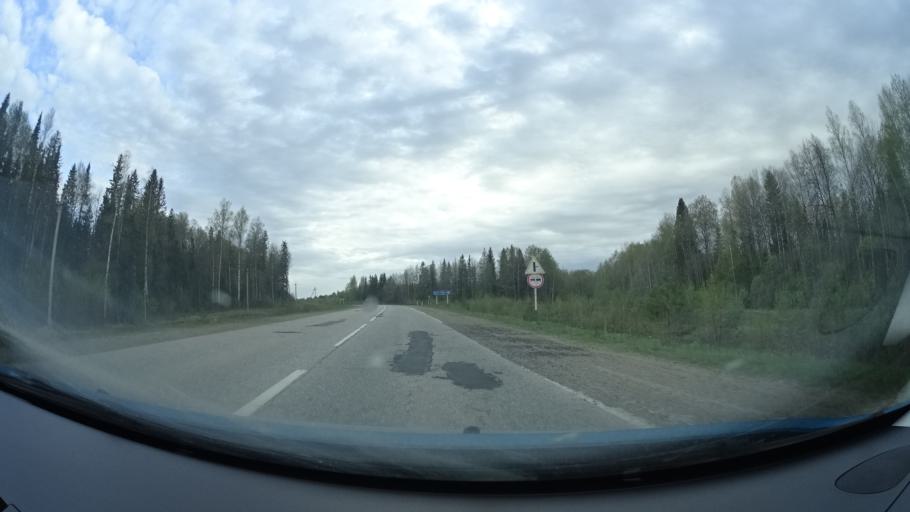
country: RU
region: Perm
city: Osa
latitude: 57.4328
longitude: 55.6241
